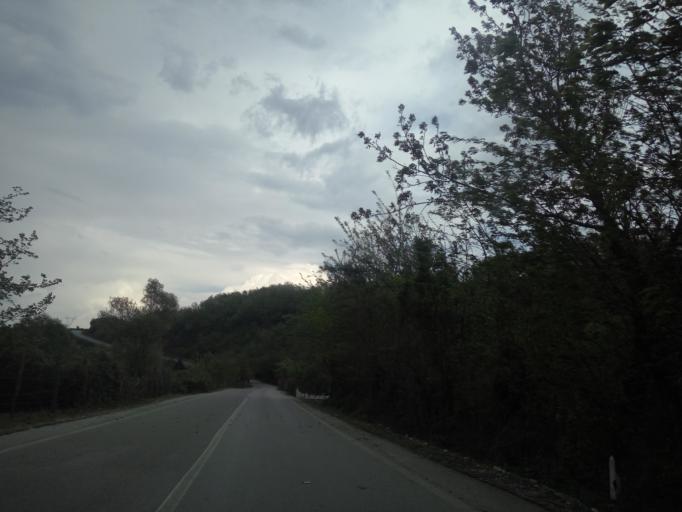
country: AL
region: Kukes
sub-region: Rrethi i Tropojes
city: Bujan
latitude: 42.3278
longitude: 20.0816
